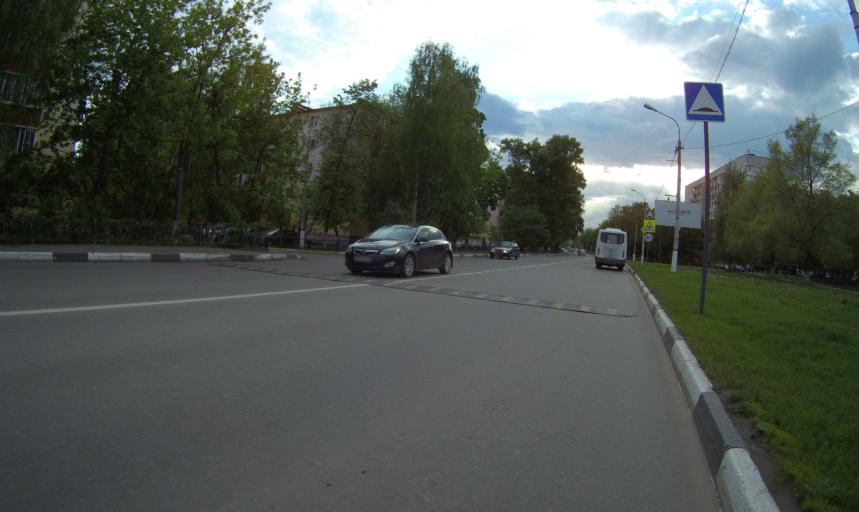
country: RU
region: Moskovskaya
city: Ramenskoye
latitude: 55.5711
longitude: 38.2442
